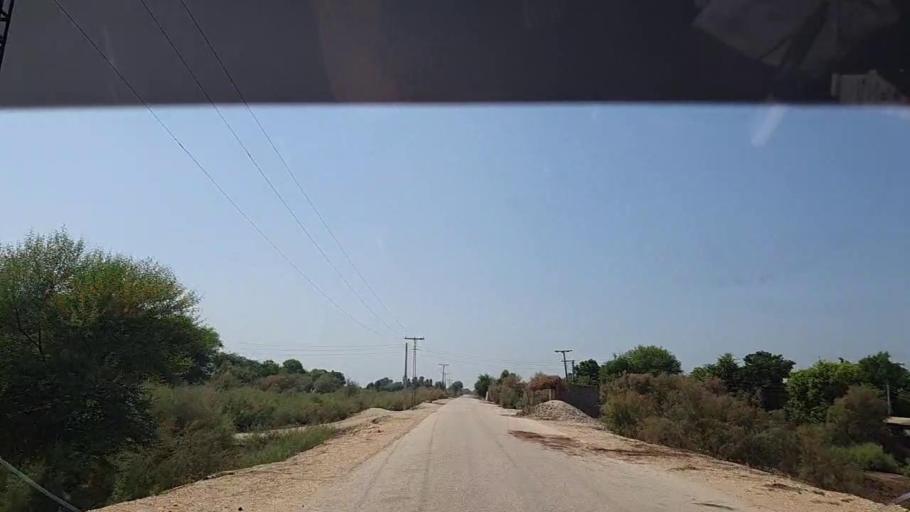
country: PK
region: Sindh
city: Ghauspur
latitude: 28.1570
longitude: 69.1516
